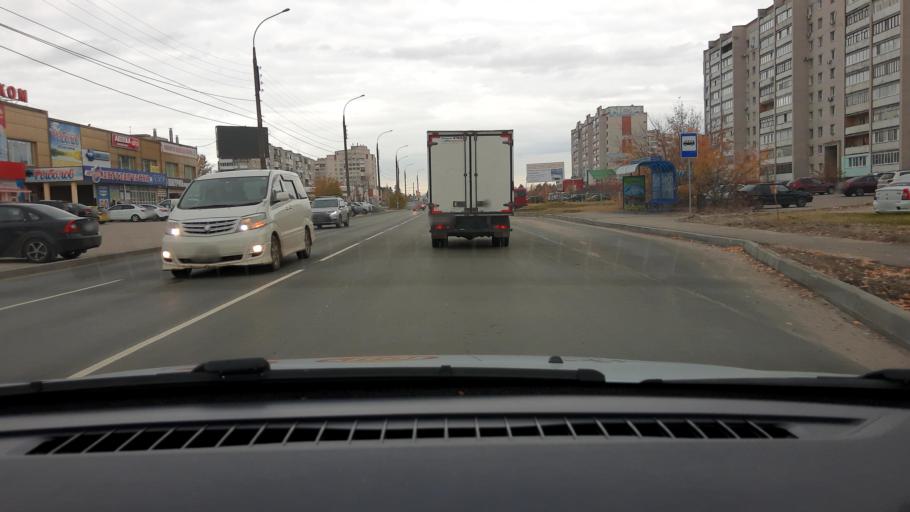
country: RU
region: Nizjnij Novgorod
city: Dzerzhinsk
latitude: 56.2312
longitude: 43.4105
